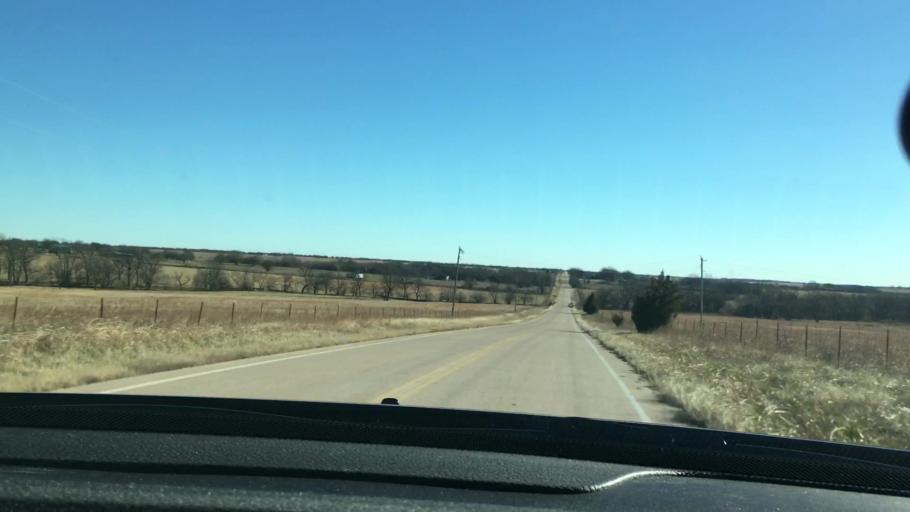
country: US
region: Oklahoma
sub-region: Marshall County
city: Madill
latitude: 34.1144
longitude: -96.7211
